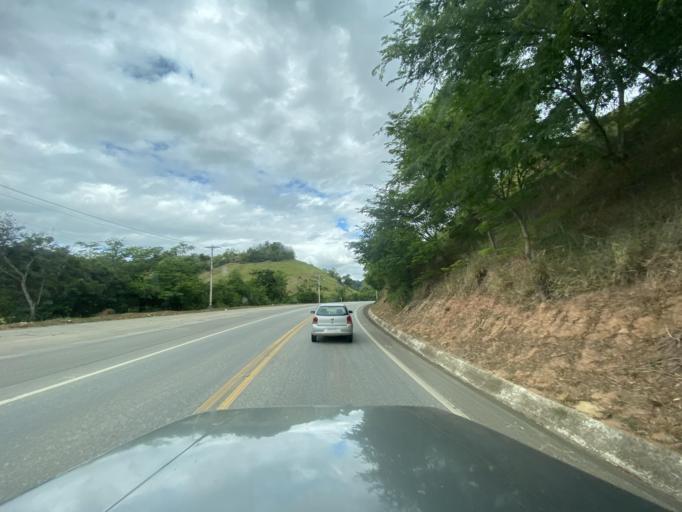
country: BR
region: Espirito Santo
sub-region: Jeronimo Monteiro
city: Jeronimo Monteiro
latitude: -20.7637
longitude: -41.4480
